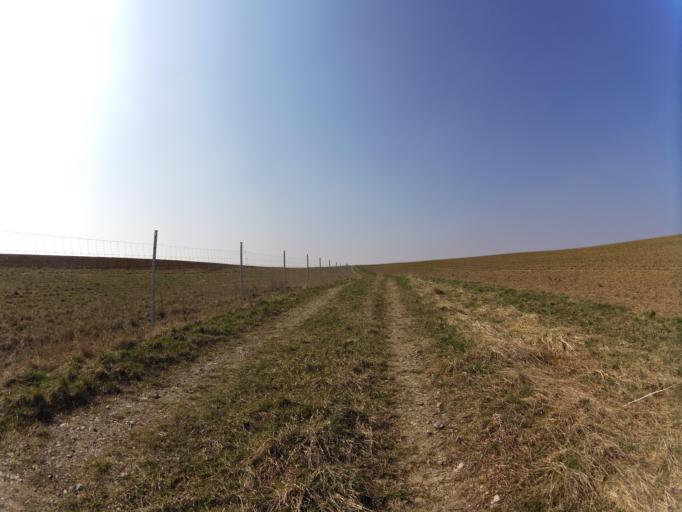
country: DE
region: Bavaria
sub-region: Regierungsbezirk Unterfranken
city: Winterhausen
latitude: 49.6760
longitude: 9.9845
